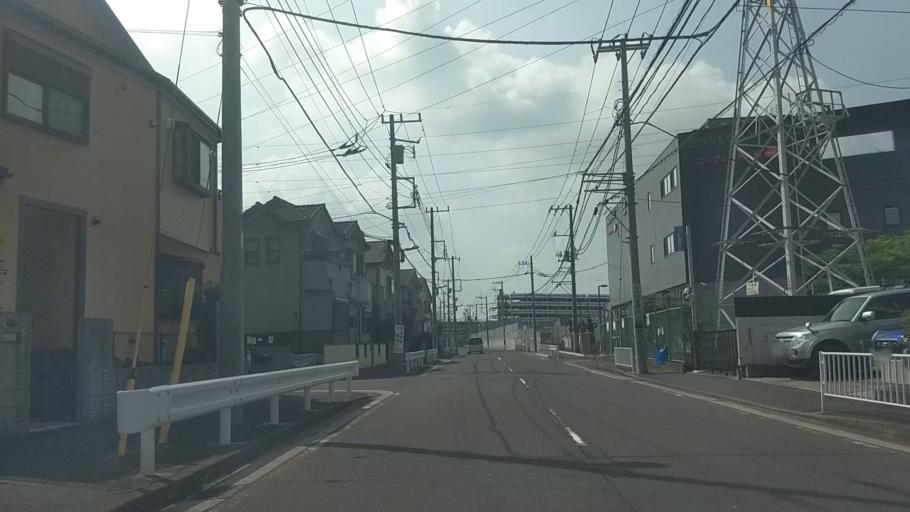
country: JP
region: Kanagawa
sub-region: Kawasaki-shi
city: Kawasaki
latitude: 35.5273
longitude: 139.6787
